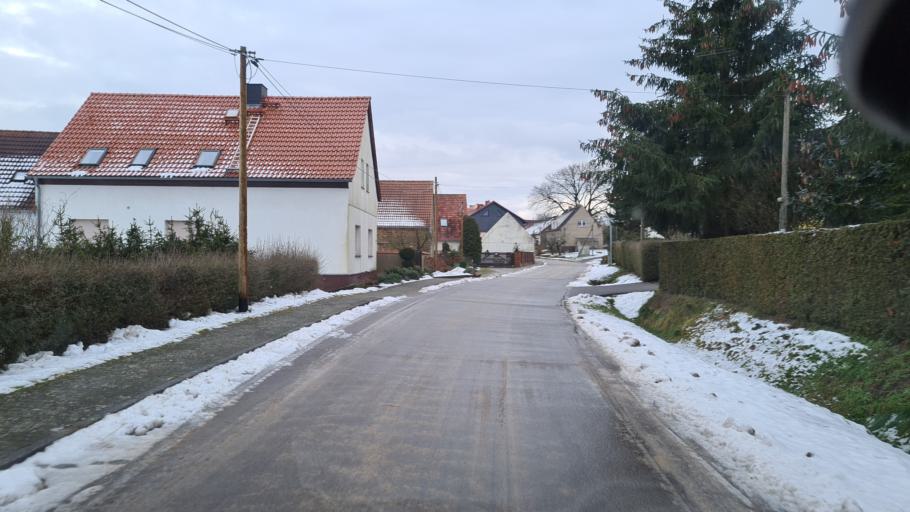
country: DE
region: Brandenburg
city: Schenkendobern
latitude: 51.9111
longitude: 14.5749
